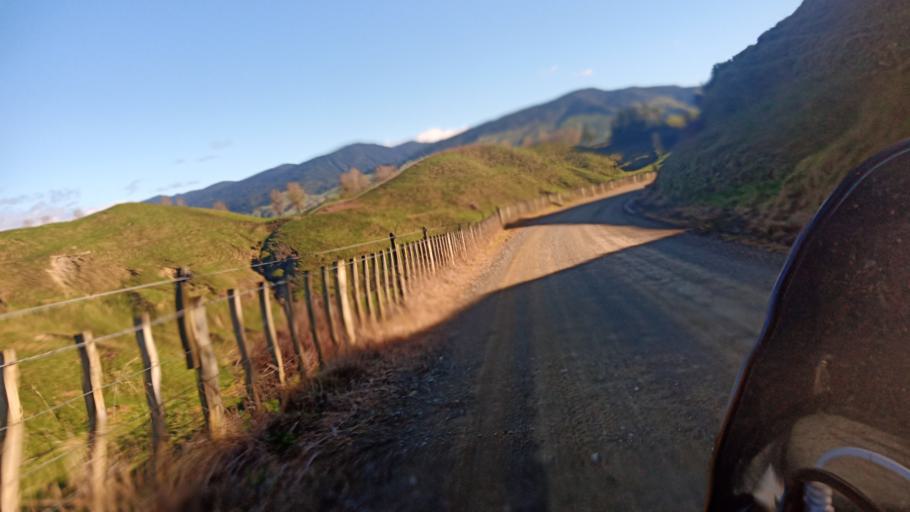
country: NZ
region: Hawke's Bay
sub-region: Wairoa District
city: Wairoa
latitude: -38.7908
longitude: 177.2750
